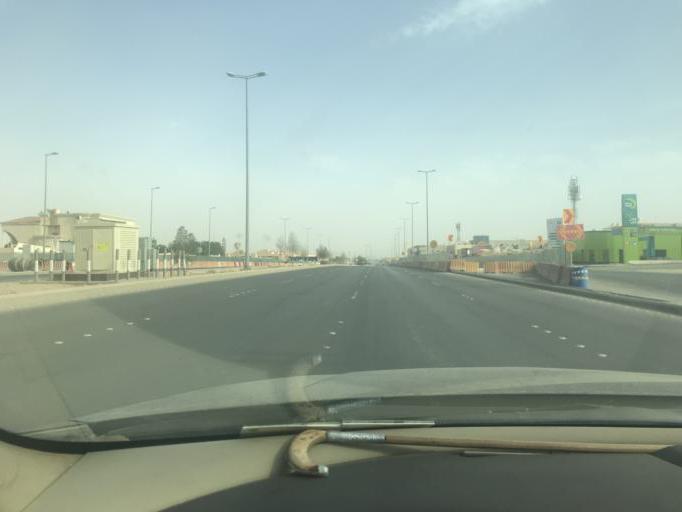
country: SA
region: Ar Riyad
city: Riyadh
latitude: 24.8223
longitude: 46.6855
